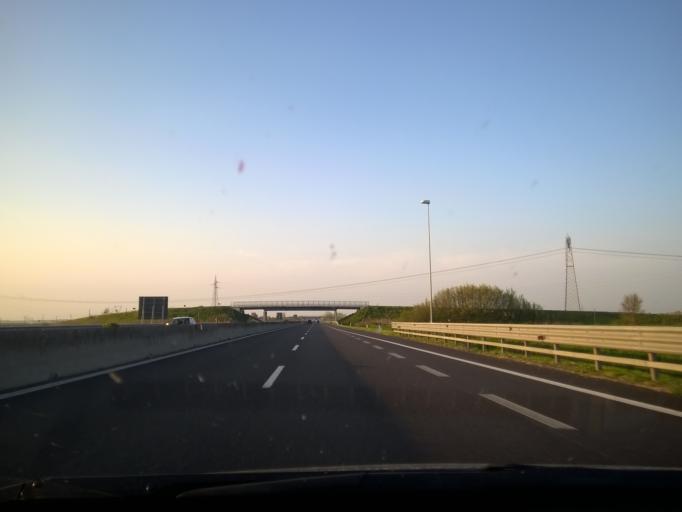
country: IT
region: Emilia-Romagna
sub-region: Provincia di Ferrara
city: Porotto-Cassama
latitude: 44.8838
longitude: 11.5701
